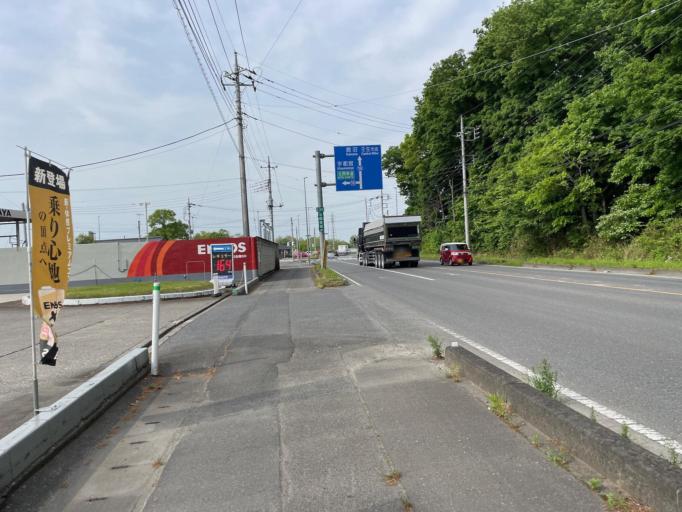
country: JP
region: Tochigi
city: Mibu
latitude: 36.4051
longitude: 139.8039
